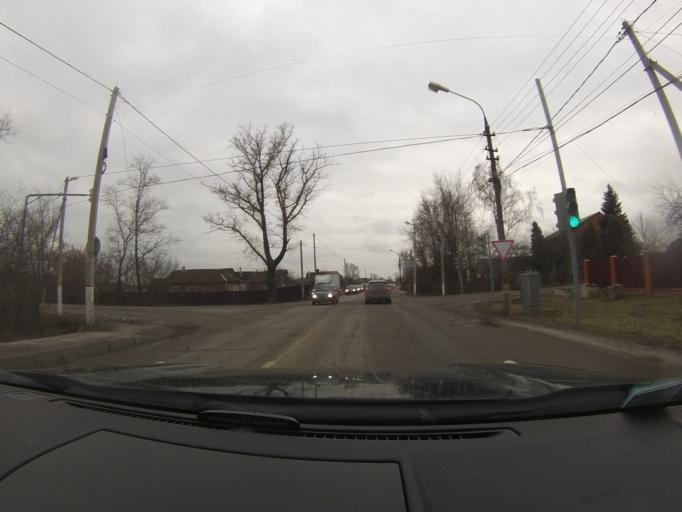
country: RU
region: Moskovskaya
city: Lopatinskiy
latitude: 55.3307
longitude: 38.7119
